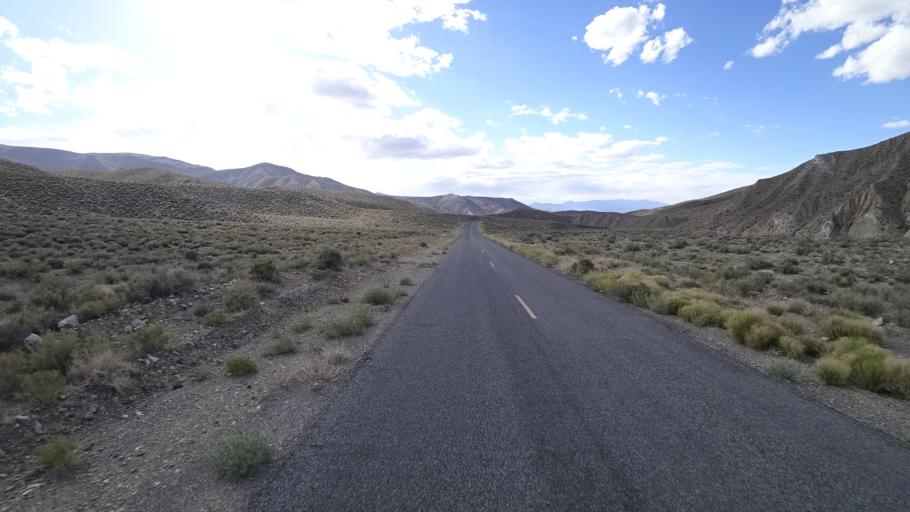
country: US
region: Nevada
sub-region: Nye County
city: Beatty
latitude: 36.4094
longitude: -117.1742
